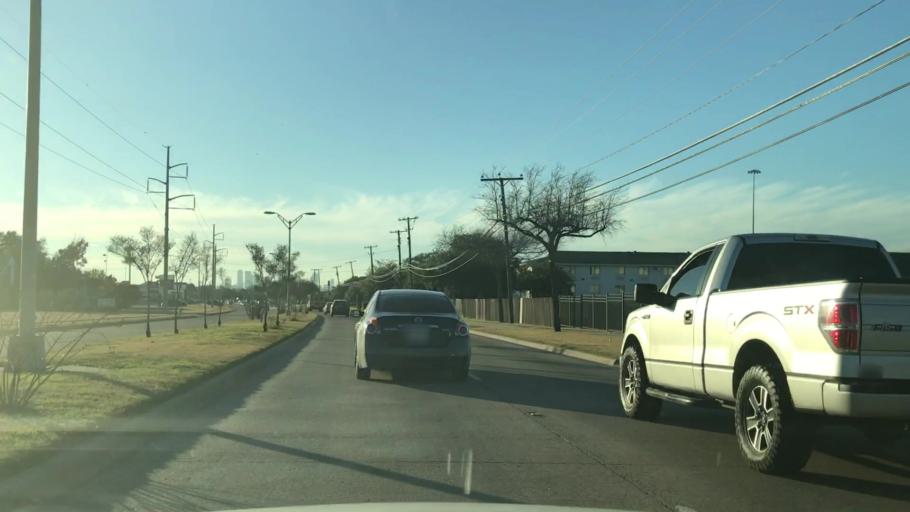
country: US
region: Texas
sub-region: Dallas County
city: Balch Springs
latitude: 32.7927
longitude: -96.6943
